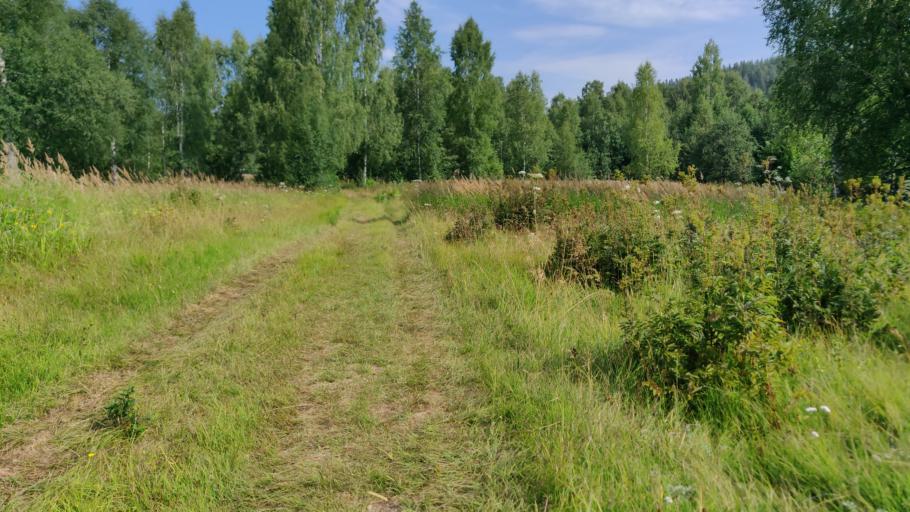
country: SE
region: Vaermland
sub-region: Hagfors Kommun
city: Hagfors
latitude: 60.0352
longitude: 13.5945
